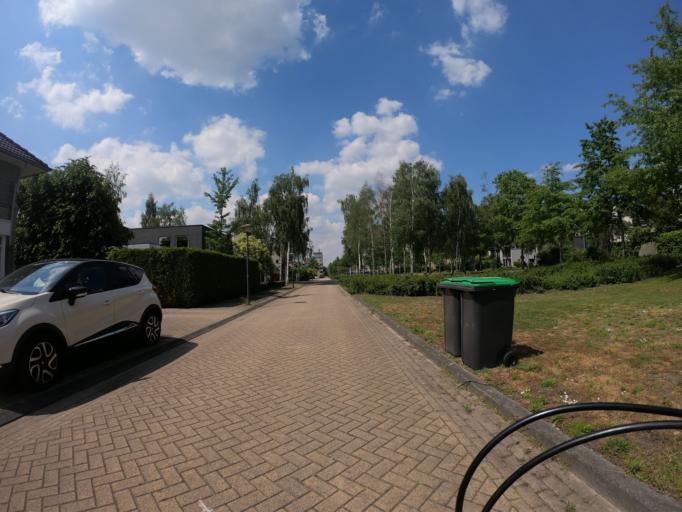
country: NL
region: North Brabant
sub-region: Gemeente Uden
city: Uden
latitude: 51.6430
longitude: 5.6215
